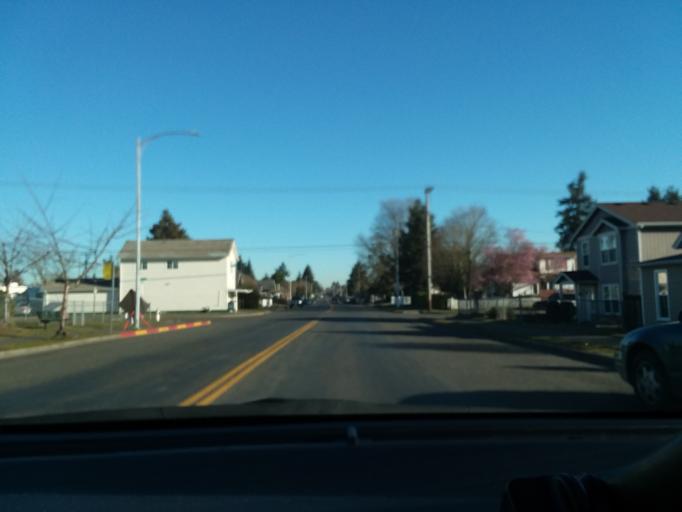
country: US
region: Washington
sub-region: Pierce County
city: Lakewood
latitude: 47.1988
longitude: -122.4723
